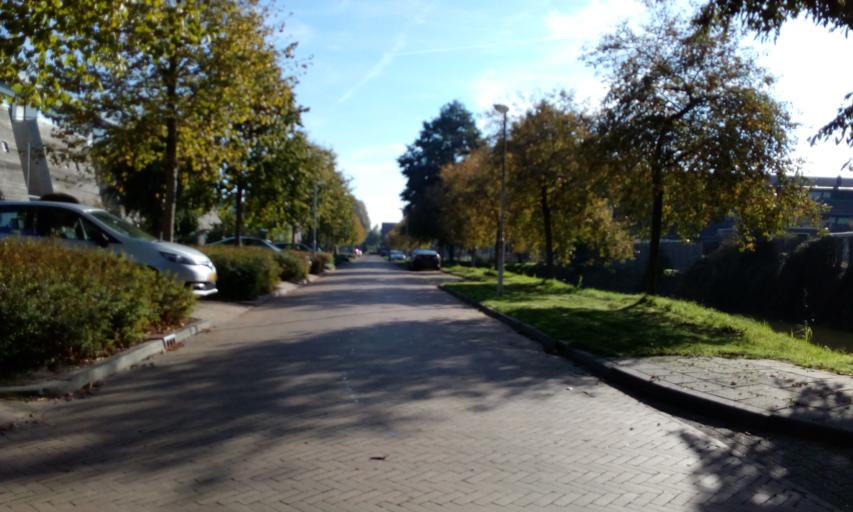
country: NL
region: Utrecht
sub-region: Stichtse Vecht
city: Spechtenkamp
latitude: 52.1093
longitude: 5.0181
